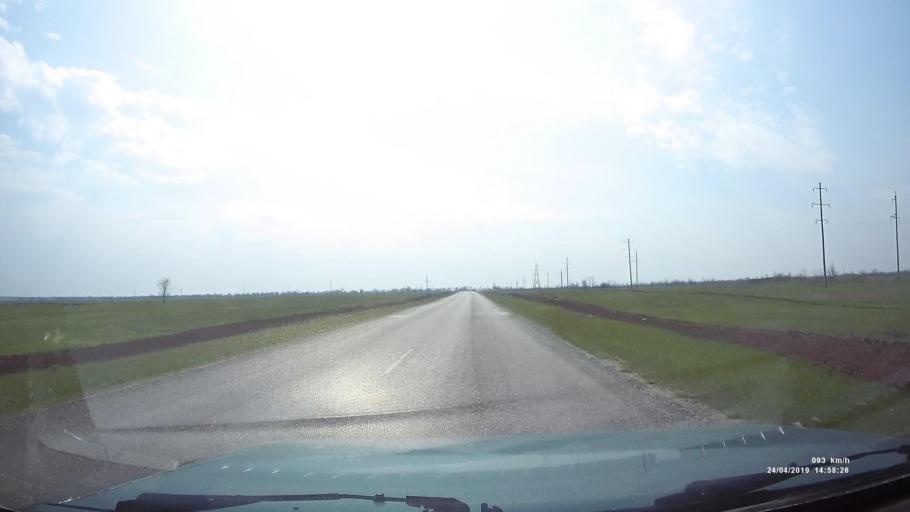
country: RU
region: Rostov
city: Remontnoye
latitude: 46.5692
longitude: 43.5980
